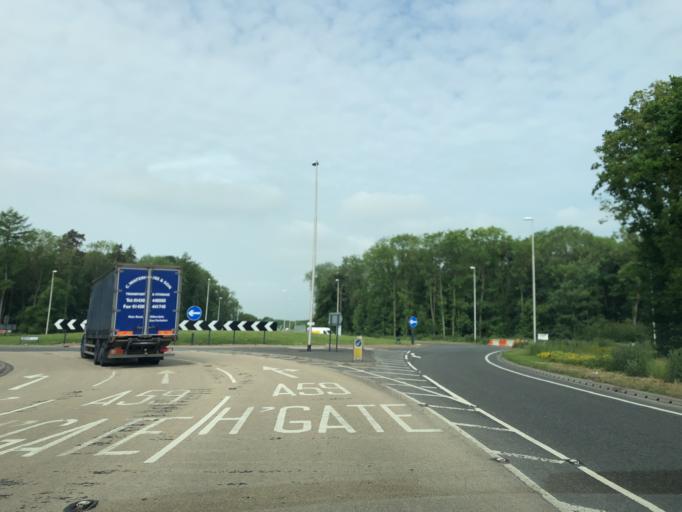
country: GB
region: England
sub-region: City and Borough of Leeds
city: Wetherby
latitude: 54.0097
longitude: -1.3856
